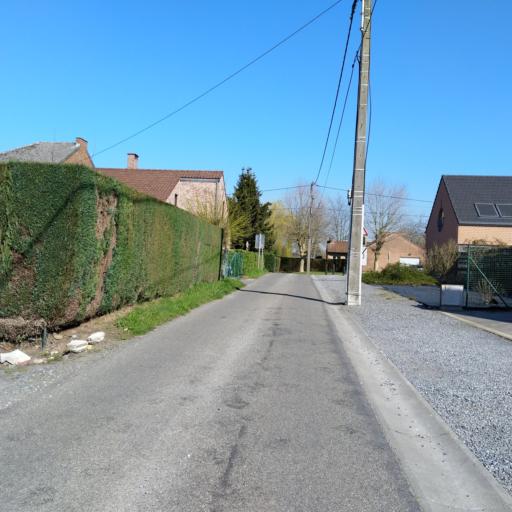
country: BE
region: Wallonia
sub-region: Province du Hainaut
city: Jurbise
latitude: 50.5089
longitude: 3.9397
